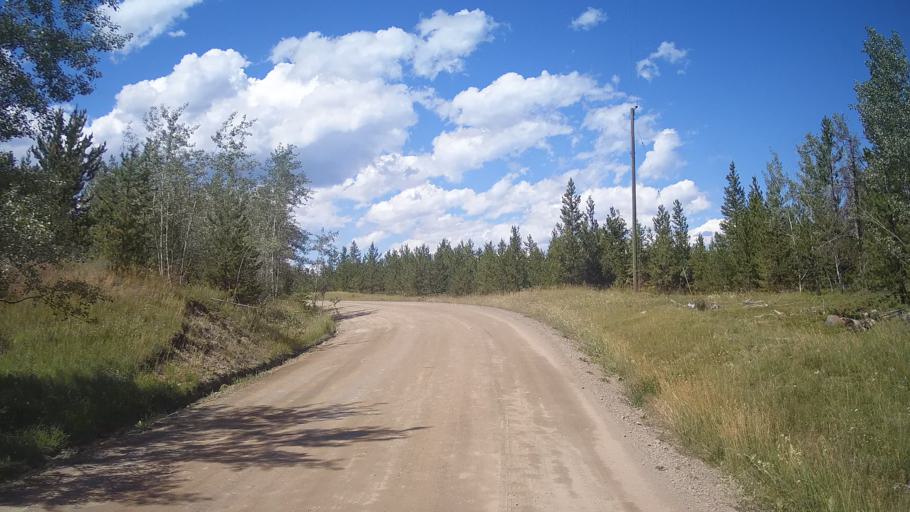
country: CA
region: British Columbia
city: Cache Creek
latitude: 51.2687
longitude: -121.7084
